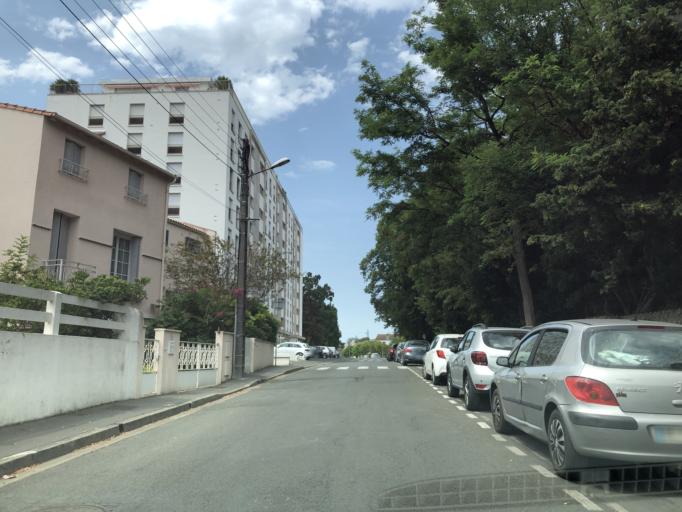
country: FR
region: Poitou-Charentes
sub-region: Departement de la Charente-Maritime
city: Royan
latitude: 45.6239
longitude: -1.0354
